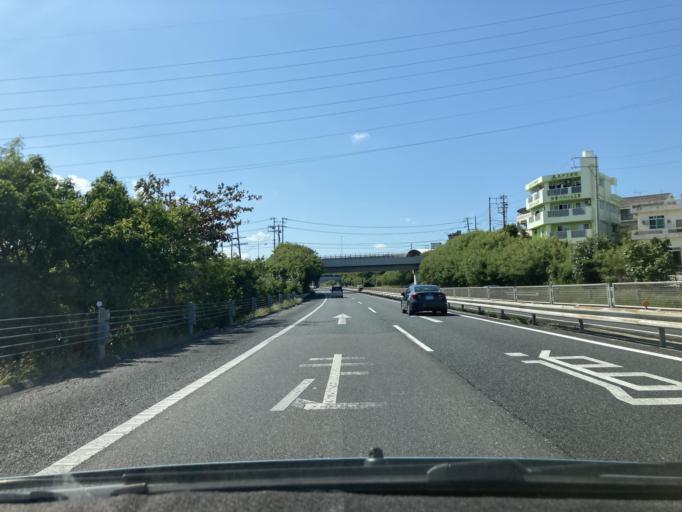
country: JP
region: Okinawa
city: Ginowan
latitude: 26.2430
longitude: 127.7444
